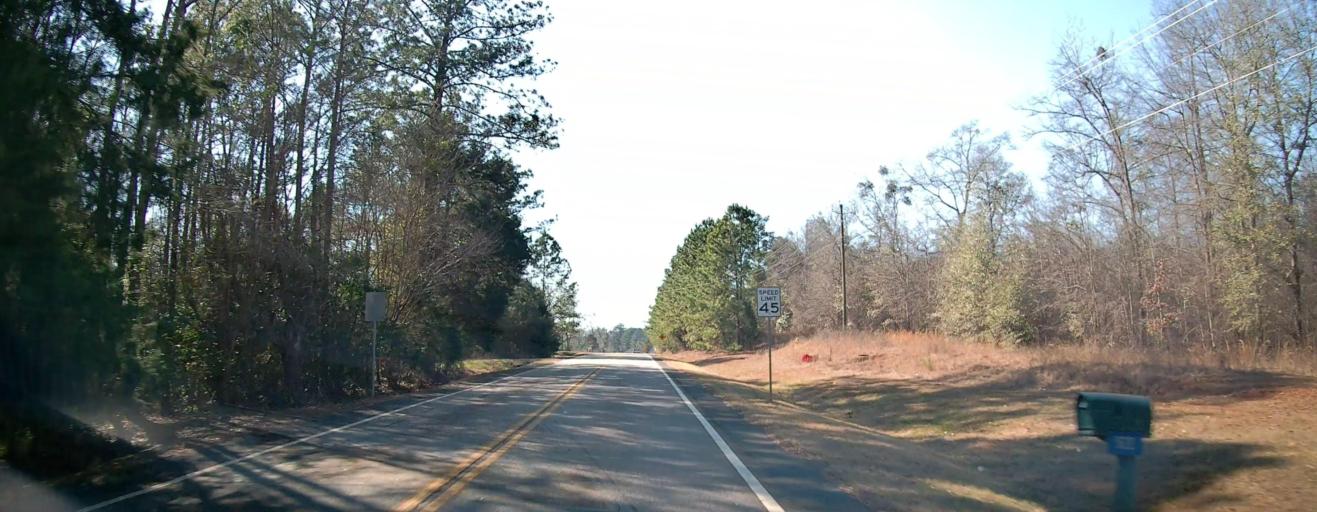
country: US
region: Georgia
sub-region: Macon County
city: Oglethorpe
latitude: 32.1965
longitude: -84.1500
